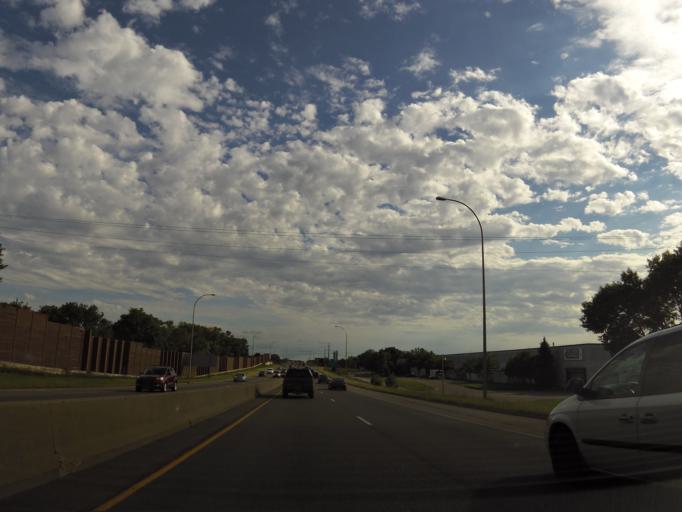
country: US
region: Minnesota
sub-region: Hennepin County
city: New Hope
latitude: 44.9984
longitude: -93.4010
